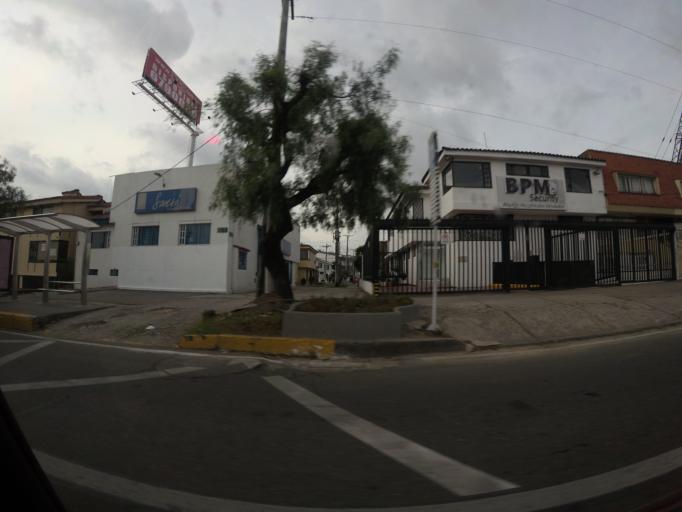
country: CO
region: Bogota D.C.
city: Barrio San Luis
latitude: 4.7106
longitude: -74.0763
